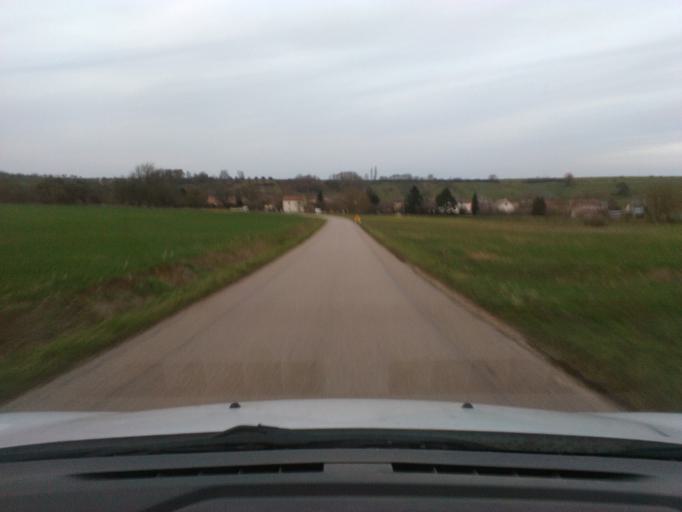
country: FR
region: Lorraine
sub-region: Departement des Vosges
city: Mirecourt
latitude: 48.3064
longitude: 6.0985
